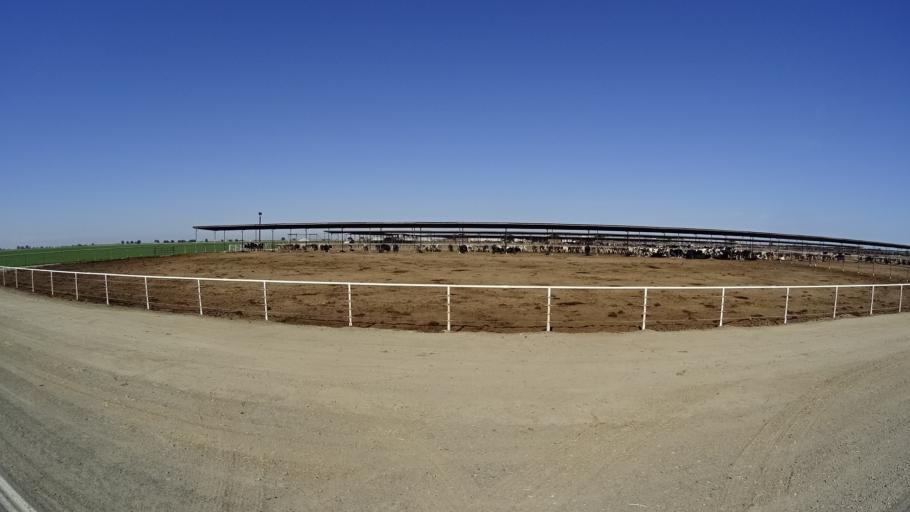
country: US
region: California
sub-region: Kings County
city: Home Garden
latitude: 36.2411
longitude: -119.5472
